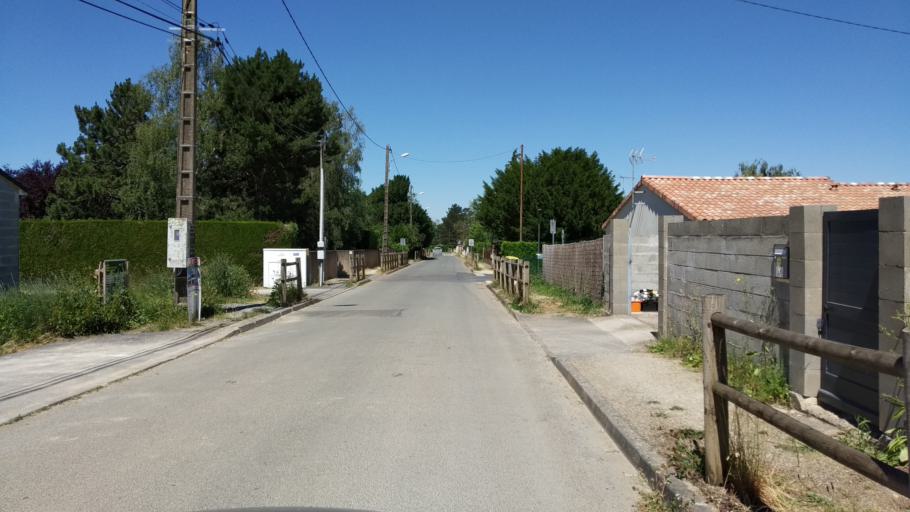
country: FR
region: Poitou-Charentes
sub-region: Departement de la Vienne
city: Vouneuil-sous-Biard
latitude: 46.5971
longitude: 0.2813
